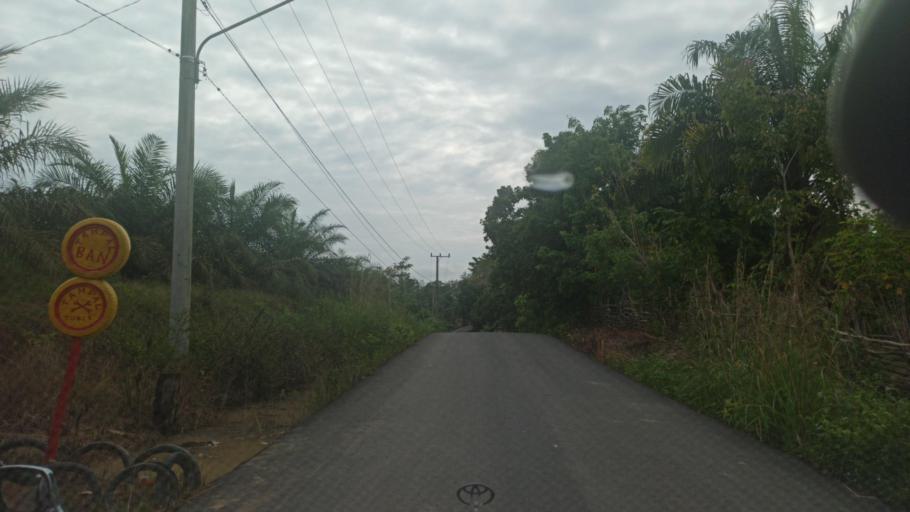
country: ID
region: South Sumatra
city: Gunungmegang Dalam
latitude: -3.2975
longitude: 103.6141
